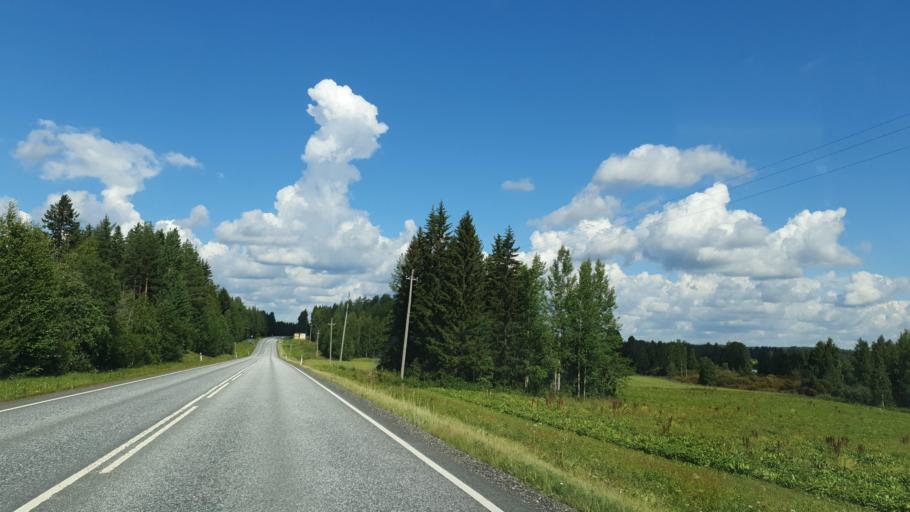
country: FI
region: Northern Savo
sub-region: Ylae-Savo
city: Sonkajaervi
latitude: 63.7998
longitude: 27.4186
